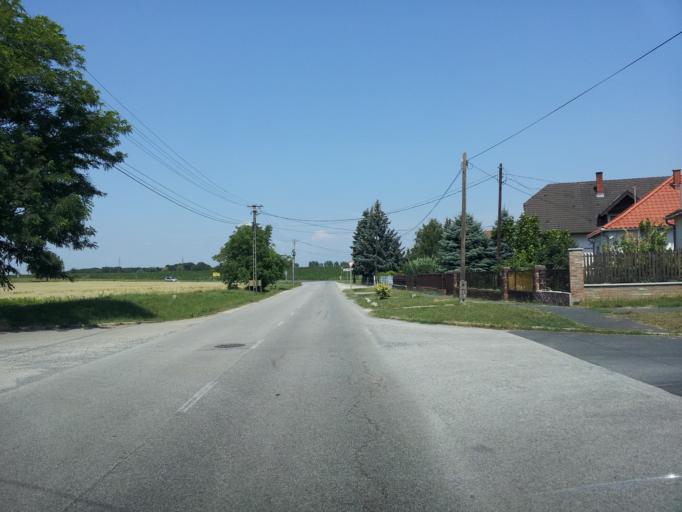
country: HU
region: Zala
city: Zalaegerszeg
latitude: 46.8564
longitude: 16.8442
